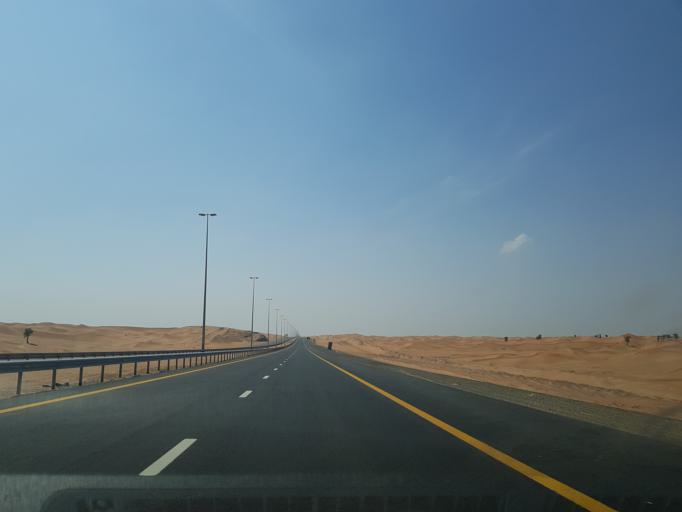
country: AE
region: Ash Shariqah
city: Adh Dhayd
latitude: 25.2508
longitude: 55.7933
